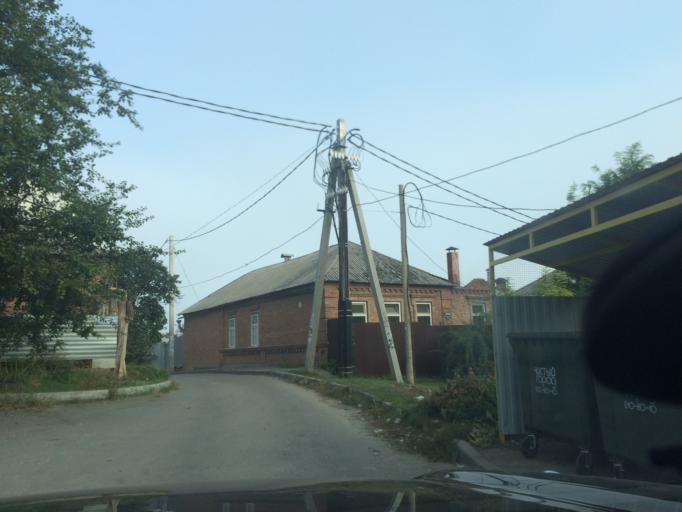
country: RU
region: Rostov
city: Rostov-na-Donu
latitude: 47.2106
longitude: 39.6924
